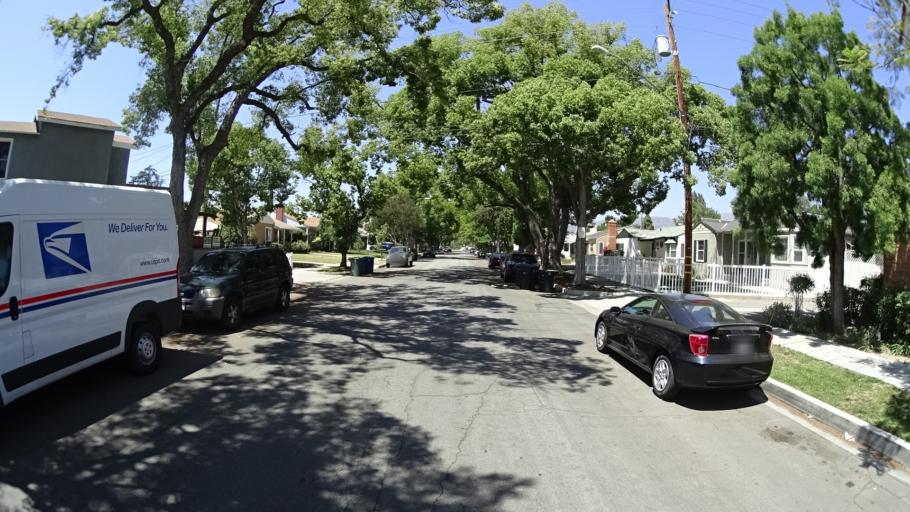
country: US
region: California
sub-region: Los Angeles County
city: Burbank
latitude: 34.1790
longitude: -118.3407
